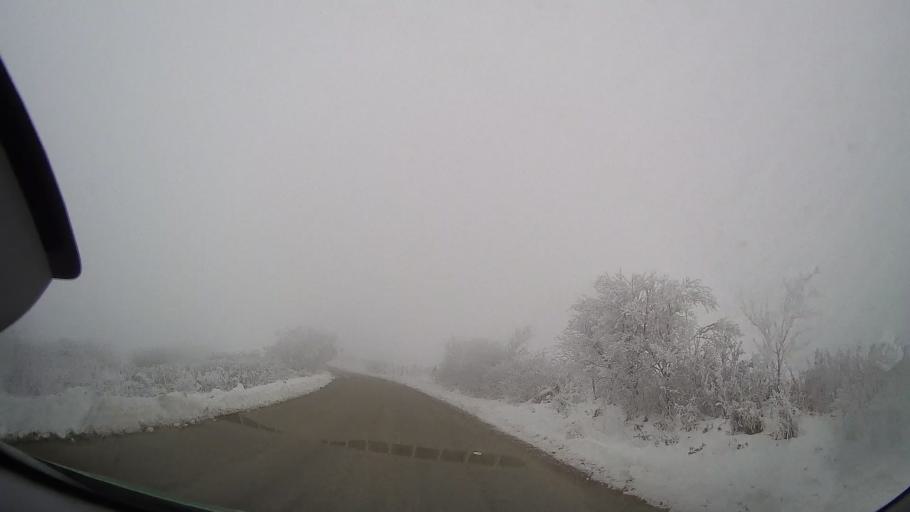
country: RO
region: Iasi
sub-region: Comuna Tansa
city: Suhulet
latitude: 46.8931
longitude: 27.2679
